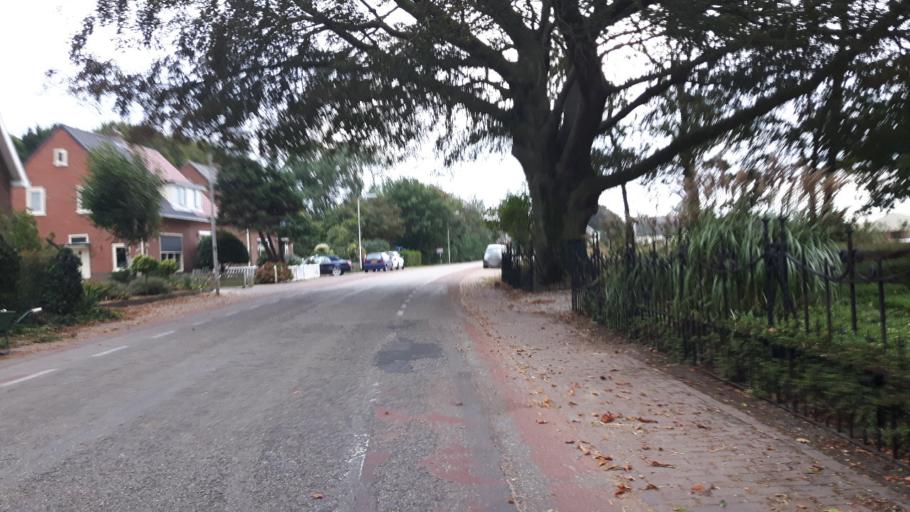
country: NL
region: South Holland
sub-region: Gemeente Hillegom
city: Hillegom
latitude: 52.3101
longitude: 4.5570
